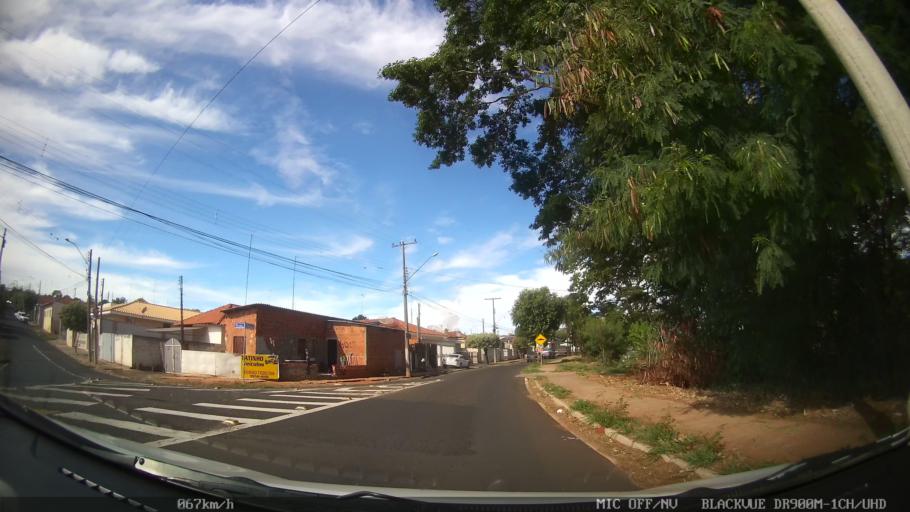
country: BR
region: Sao Paulo
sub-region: Catanduva
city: Catanduva
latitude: -21.1246
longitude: -48.9771
